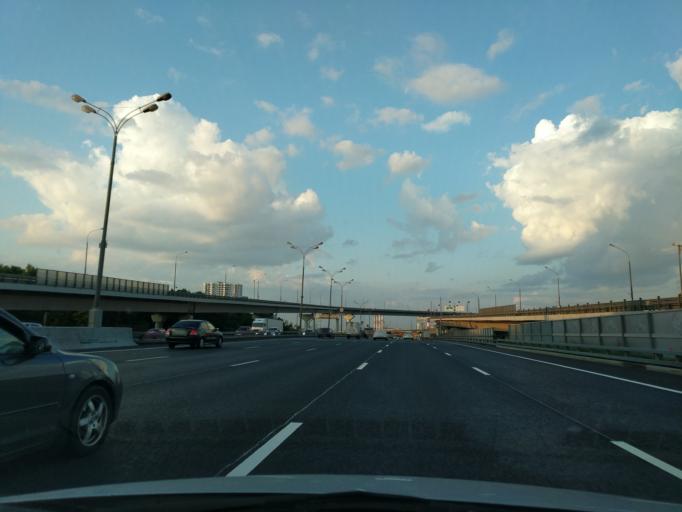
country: RU
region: Moskovskaya
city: Levoberezhnaya
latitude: 55.8833
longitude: 37.4726
